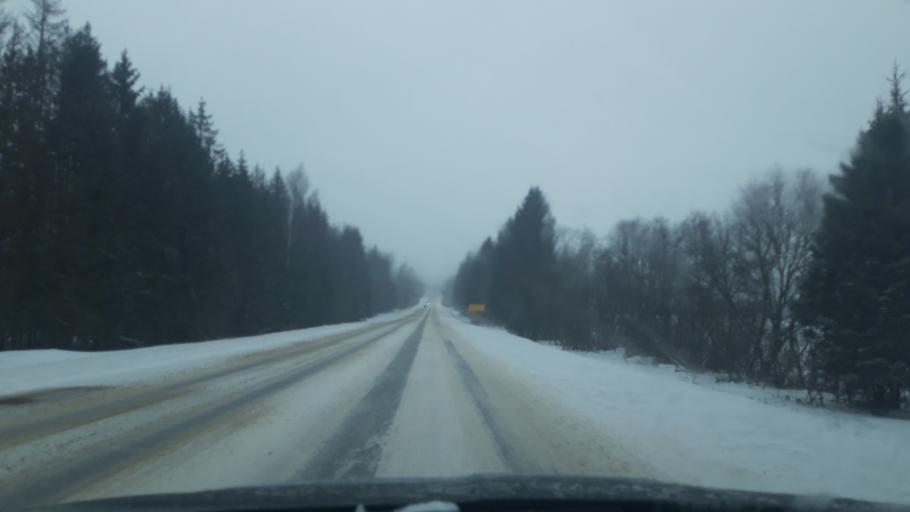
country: RU
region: Moskovskaya
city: Avtopoligon
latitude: 56.2456
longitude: 37.2394
